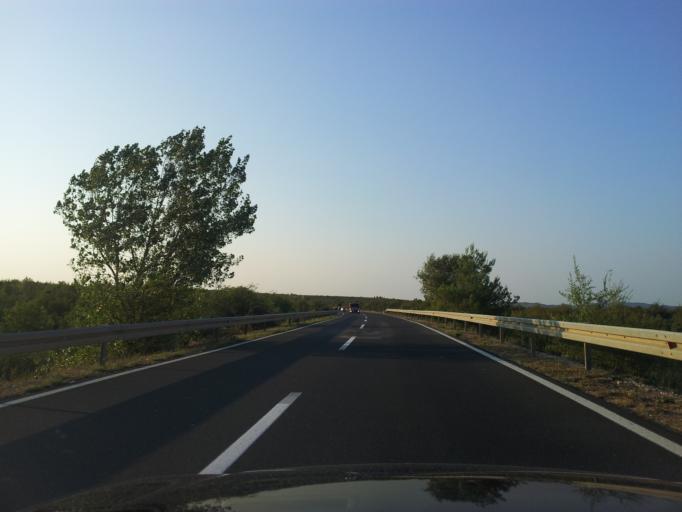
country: HR
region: Zadarska
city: Benkovac
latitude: 44.0148
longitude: 15.5691
